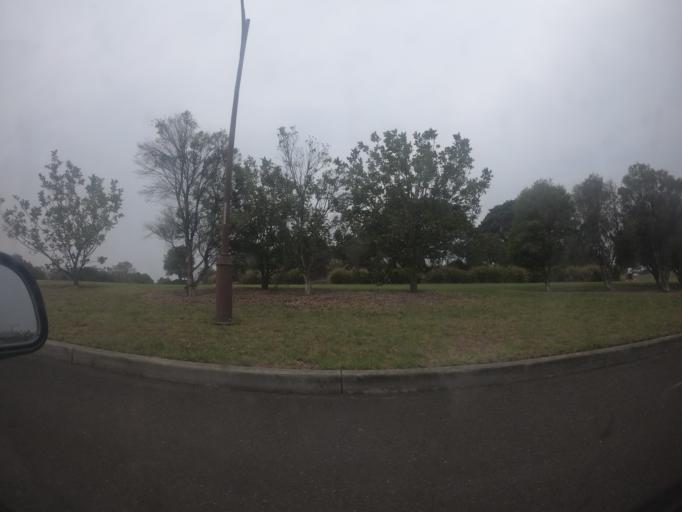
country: AU
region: New South Wales
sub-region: Shellharbour
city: Flinders
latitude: -34.5906
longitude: 150.8513
